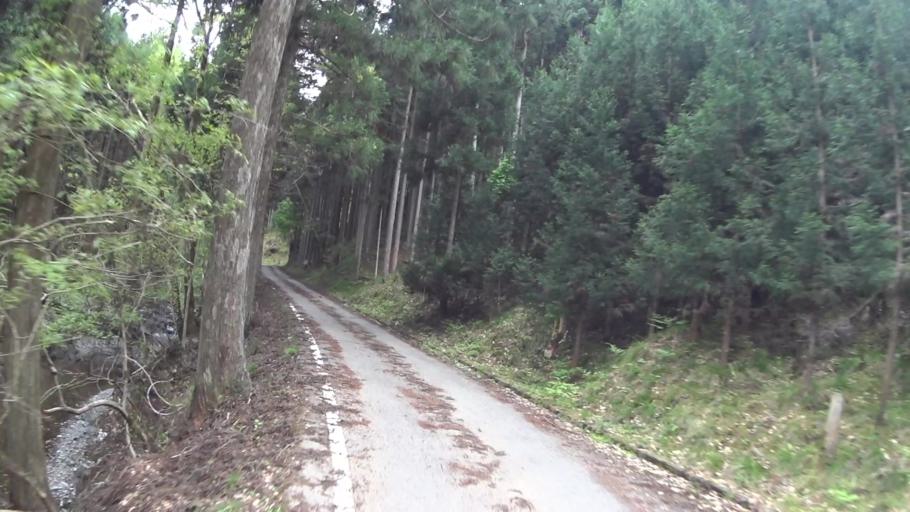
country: JP
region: Kyoto
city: Kameoka
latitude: 35.1098
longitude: 135.6322
